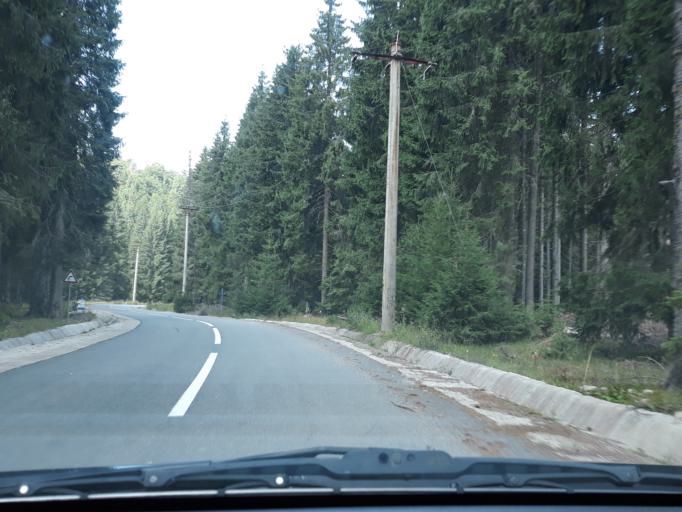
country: RO
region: Alba
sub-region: Comuna Arieseni
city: Arieseni
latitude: 46.5962
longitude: 22.7226
